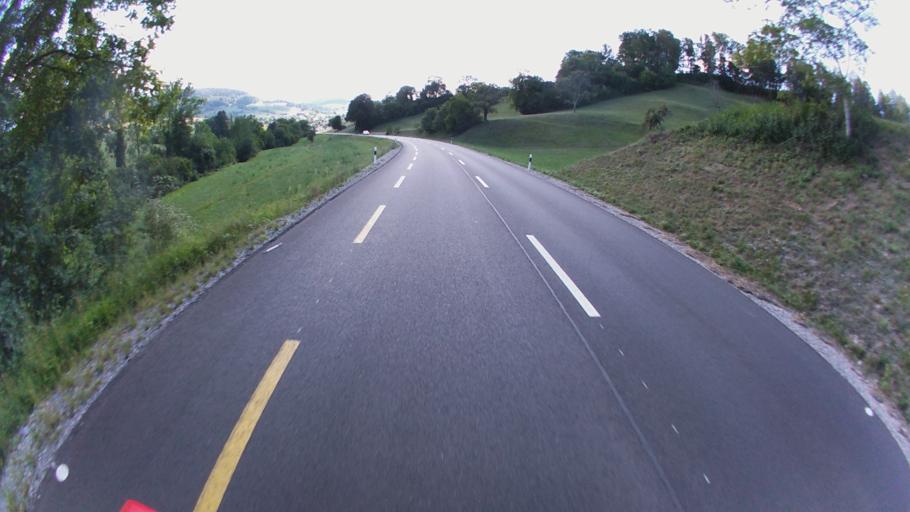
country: CH
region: Aargau
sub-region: Bezirk Rheinfelden
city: Wegenstetten
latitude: 47.5036
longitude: 7.9421
